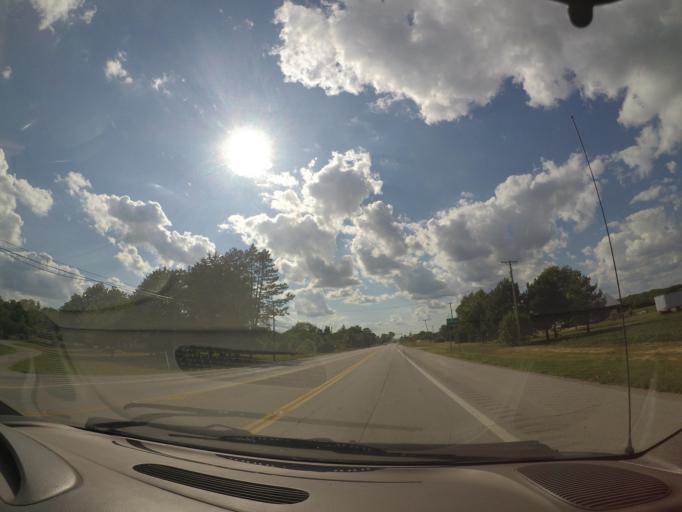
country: US
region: Ohio
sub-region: Wood County
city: Luckey
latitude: 41.4928
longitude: -83.4664
